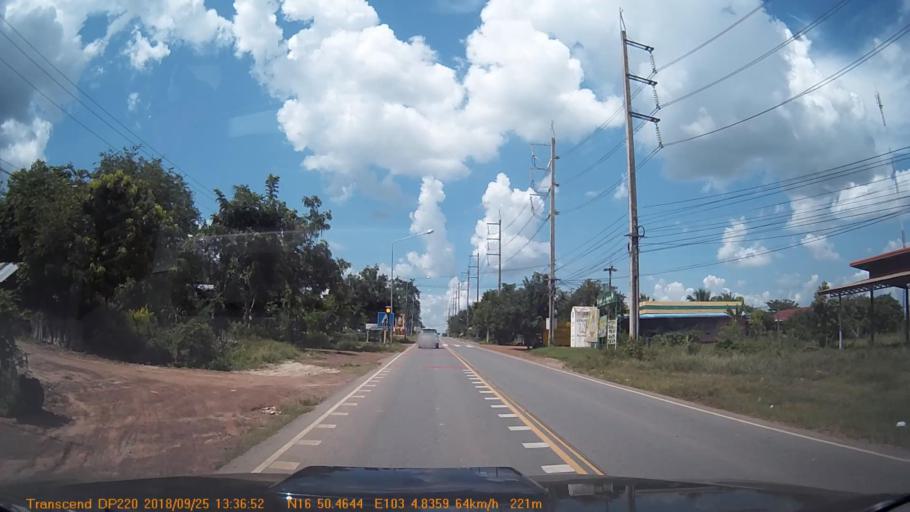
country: TH
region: Khon Kaen
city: Kranuan
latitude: 16.8412
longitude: 103.0806
